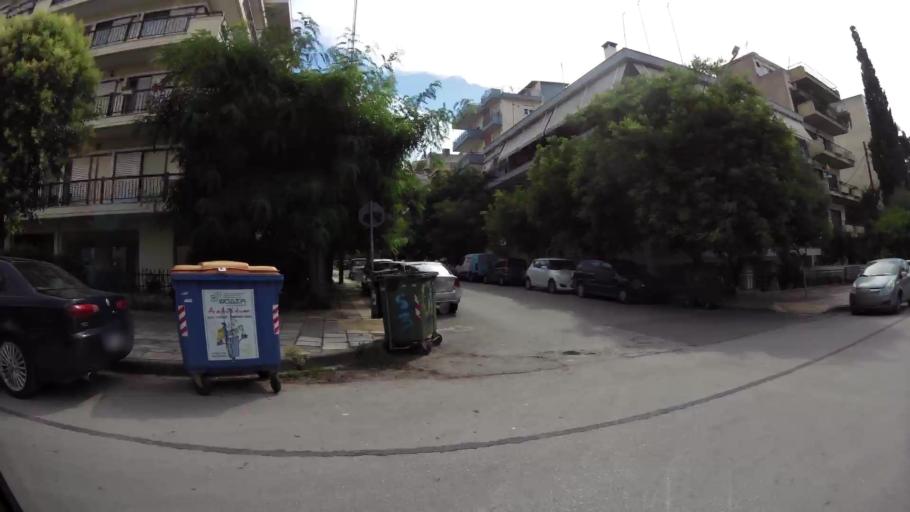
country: GR
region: Central Macedonia
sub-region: Nomos Thessalonikis
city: Kalamaria
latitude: 40.5890
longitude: 22.9498
